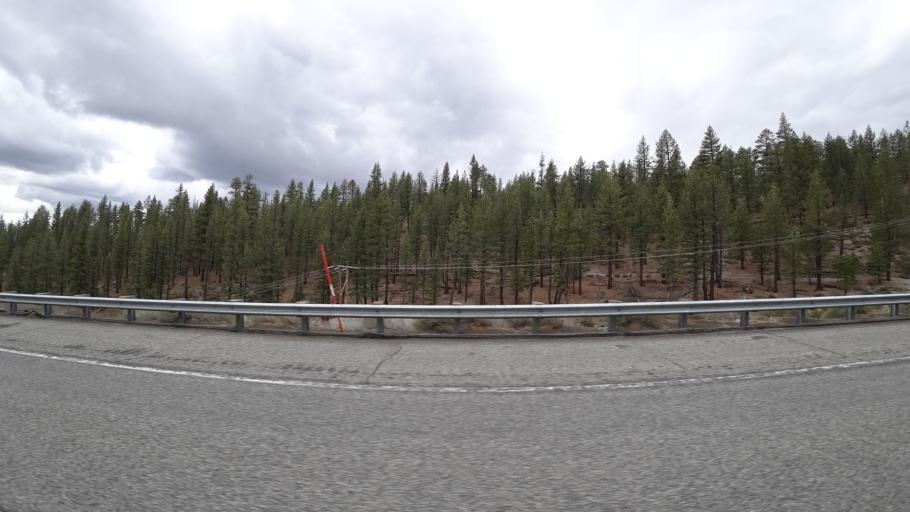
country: US
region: California
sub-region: Mono County
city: Mammoth Lakes
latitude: 37.7602
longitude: -118.9930
